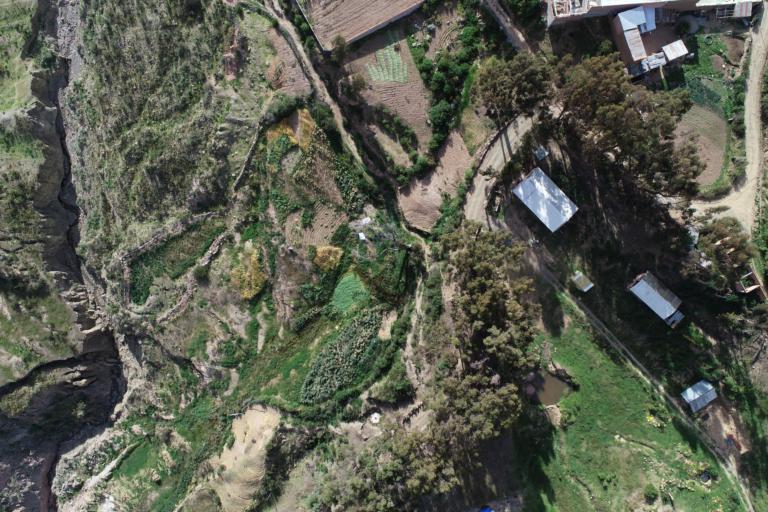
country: BO
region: La Paz
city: La Paz
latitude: -16.5498
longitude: -67.9940
